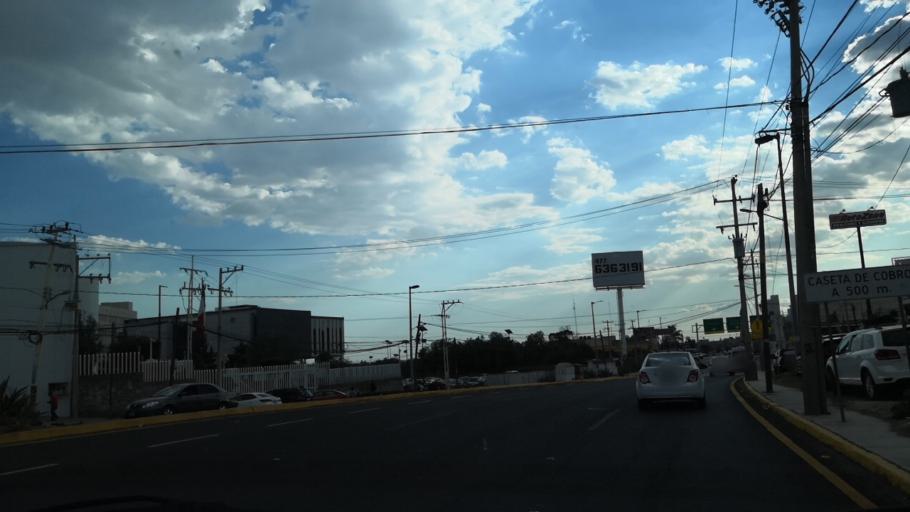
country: MX
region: Guanajuato
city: Marfil
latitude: 20.9863
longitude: -101.2865
